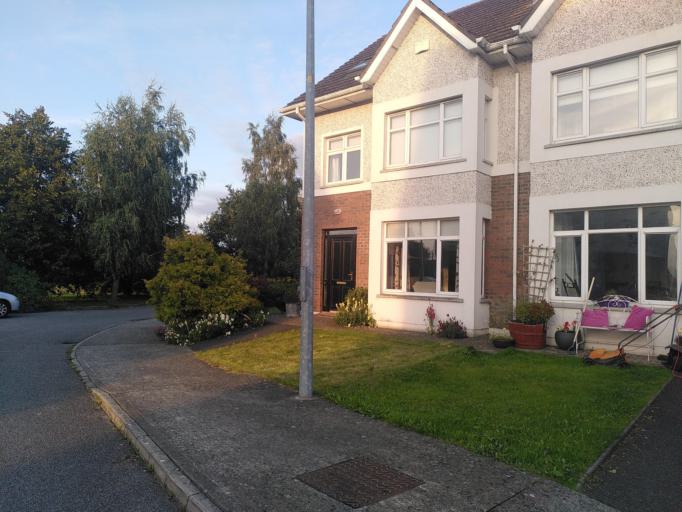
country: IE
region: Leinster
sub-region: Kilkenny
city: Kilkenny
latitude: 52.6533
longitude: -7.2641
